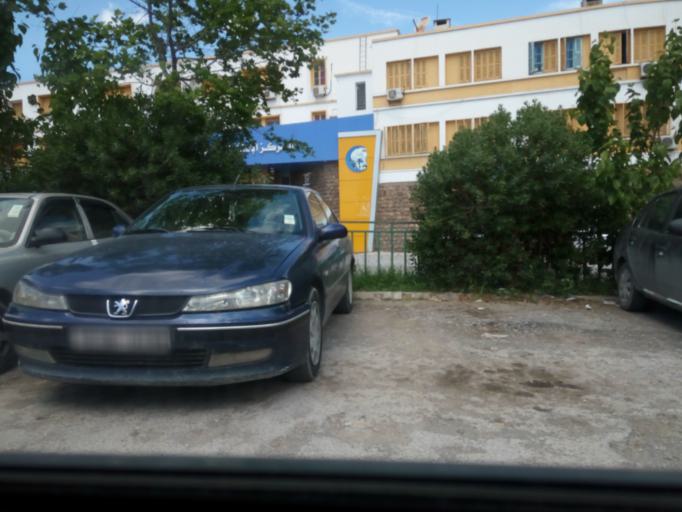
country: DZ
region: Constantine
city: Constantine
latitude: 36.3735
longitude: 6.6190
